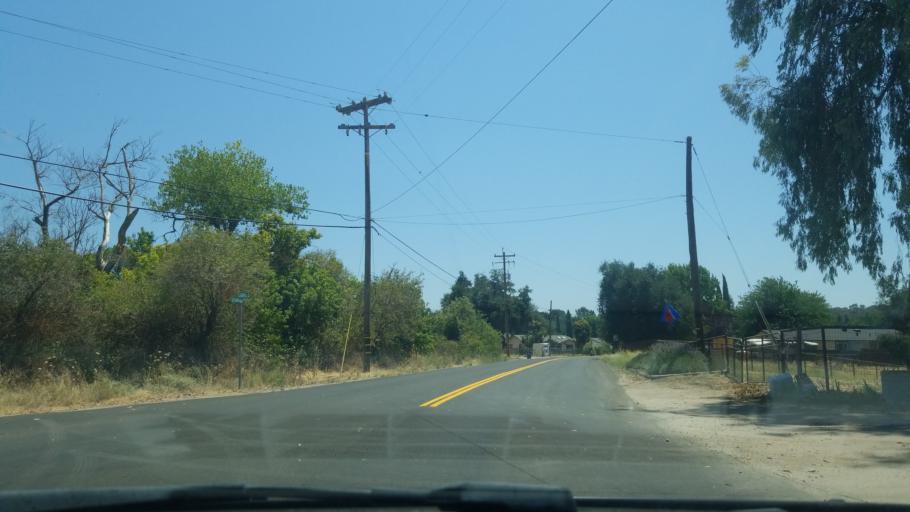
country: US
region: California
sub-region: San Luis Obispo County
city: Atascadero
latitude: 35.4926
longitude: -120.6470
